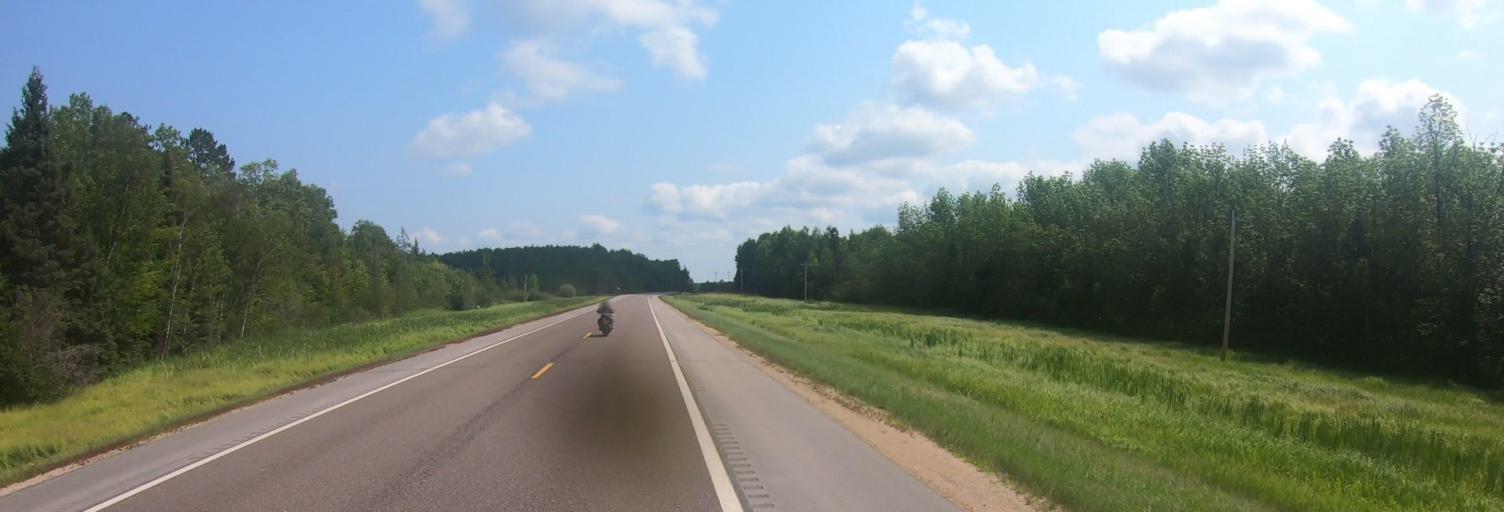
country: US
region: Minnesota
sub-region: Saint Louis County
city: Mountain Iron
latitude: 48.0544
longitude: -92.7838
